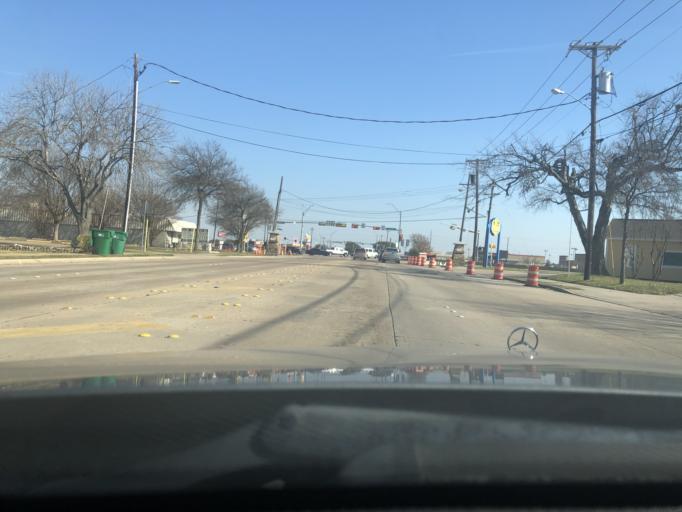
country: US
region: Texas
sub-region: Dallas County
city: Cedar Hill
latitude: 32.5900
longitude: -96.9481
